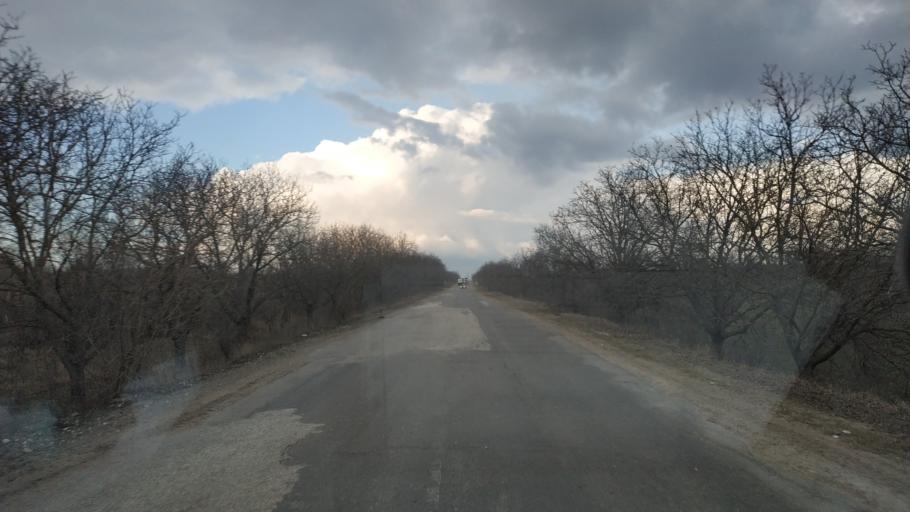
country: MD
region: Anenii Noi
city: Anenii Noi
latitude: 46.9550
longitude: 29.2830
